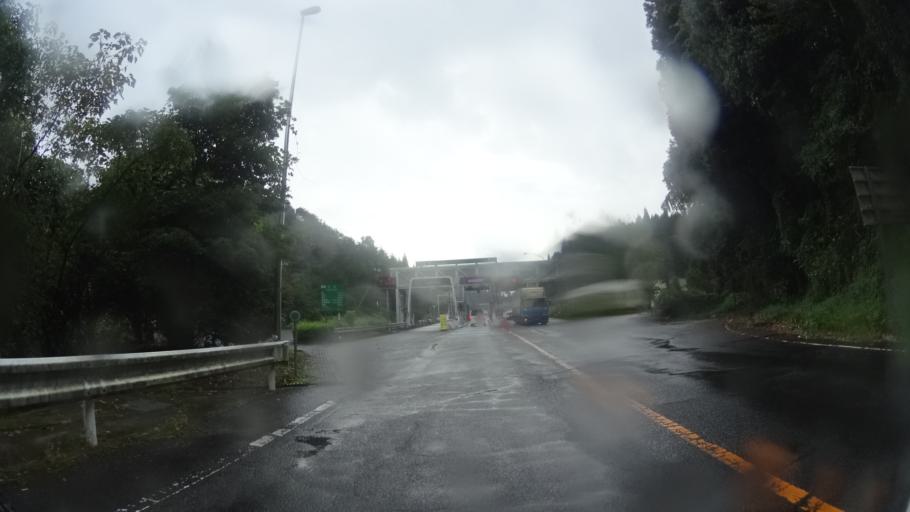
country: JP
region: Kagoshima
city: Kajiki
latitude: 31.9007
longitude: 130.7026
